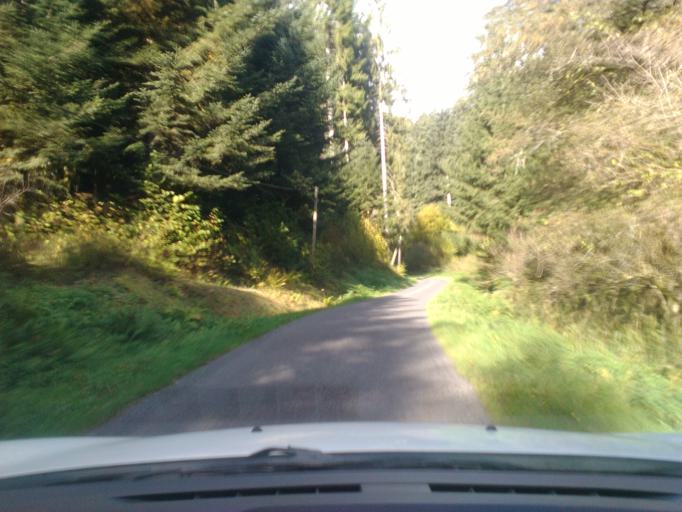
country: FR
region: Lorraine
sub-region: Departement des Vosges
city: Ban-de-Laveline
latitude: 48.2994
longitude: 7.0573
